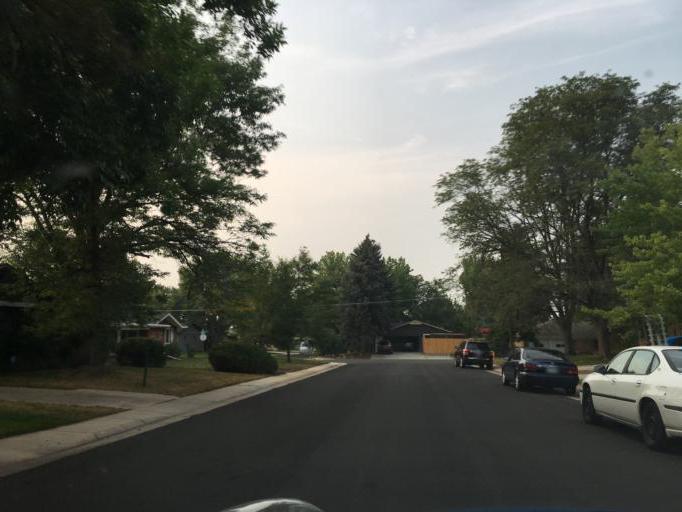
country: US
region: Colorado
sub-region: Arapahoe County
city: Glendale
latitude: 39.6869
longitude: -104.9264
